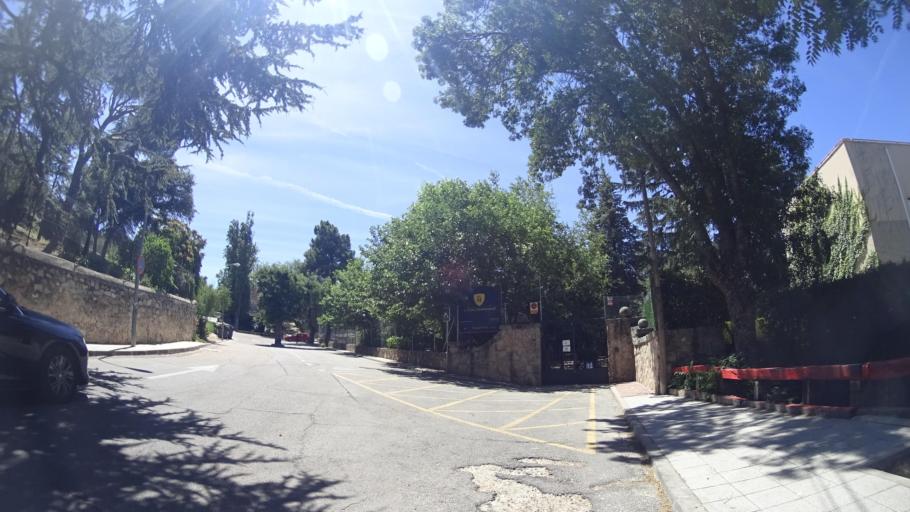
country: ES
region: Madrid
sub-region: Provincia de Madrid
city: Collado-Villalba
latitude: 40.6401
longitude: -3.9911
